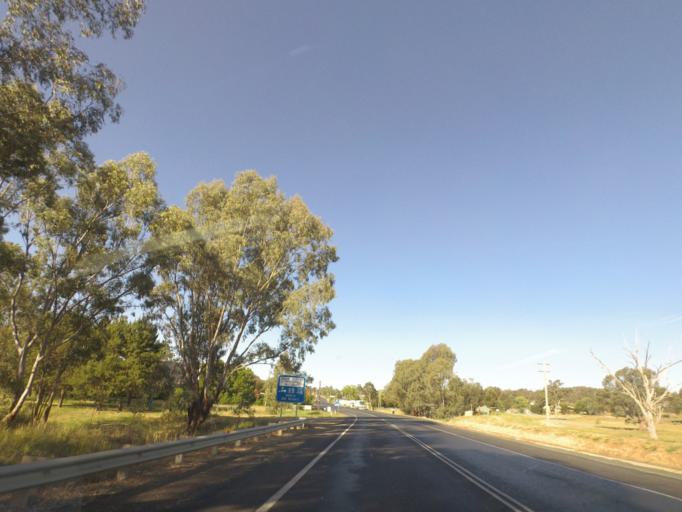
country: AU
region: New South Wales
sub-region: Wagga Wagga
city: Forest Hill
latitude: -35.2789
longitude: 147.7339
